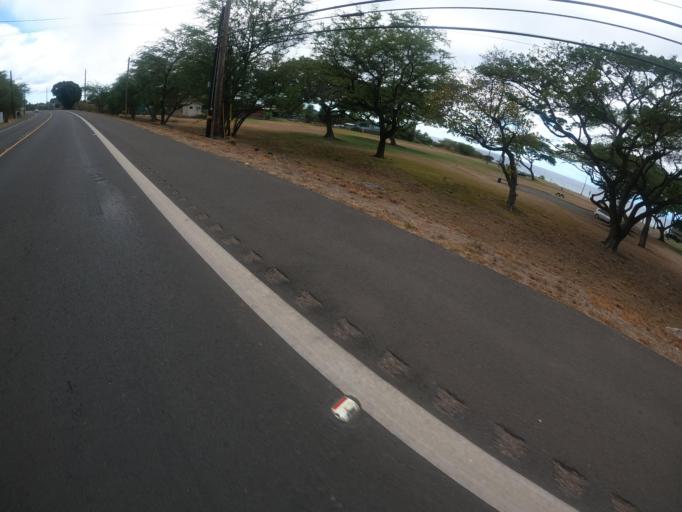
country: US
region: Hawaii
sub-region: Honolulu County
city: Makaha
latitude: 21.4844
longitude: -158.2292
